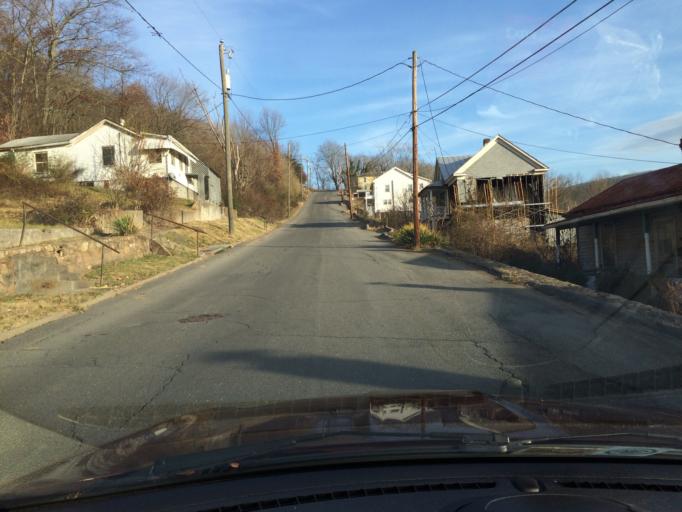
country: US
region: Virginia
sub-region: Alleghany County
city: Clifton Forge
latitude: 37.8172
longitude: -79.8195
